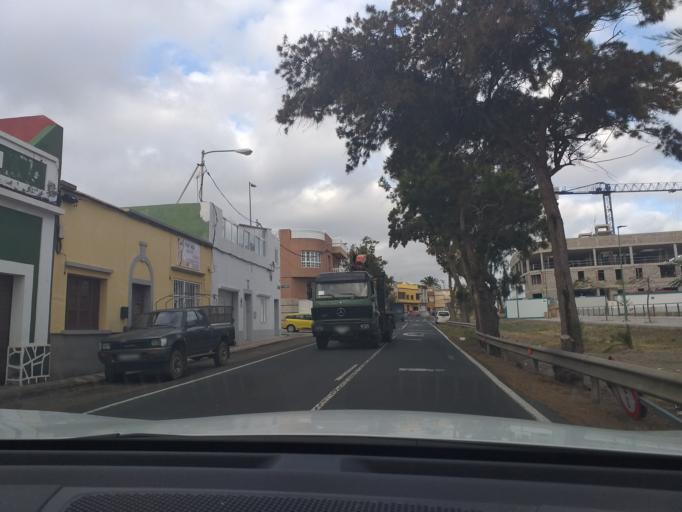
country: ES
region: Canary Islands
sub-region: Provincia de Las Palmas
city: Arucas
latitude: 28.0987
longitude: -15.4809
